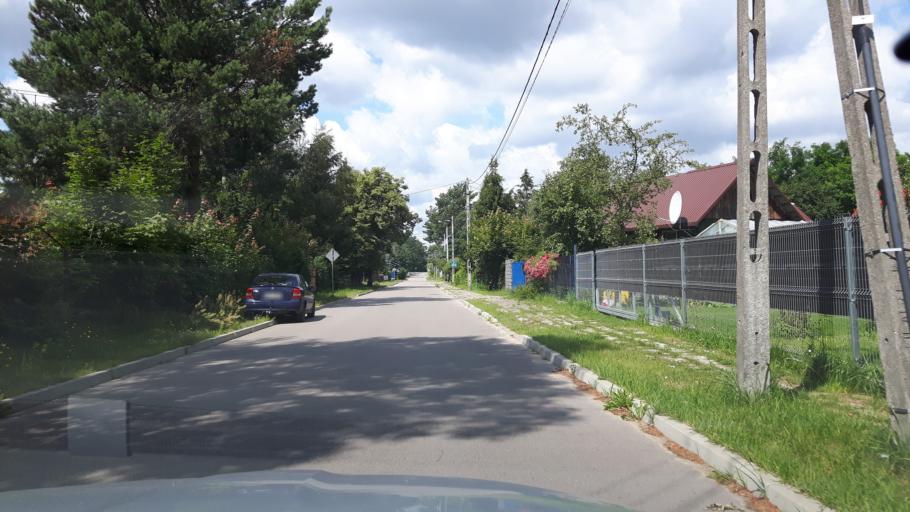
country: PL
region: Masovian Voivodeship
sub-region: Powiat ostrowski
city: Brok
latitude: 52.6999
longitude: 21.8524
